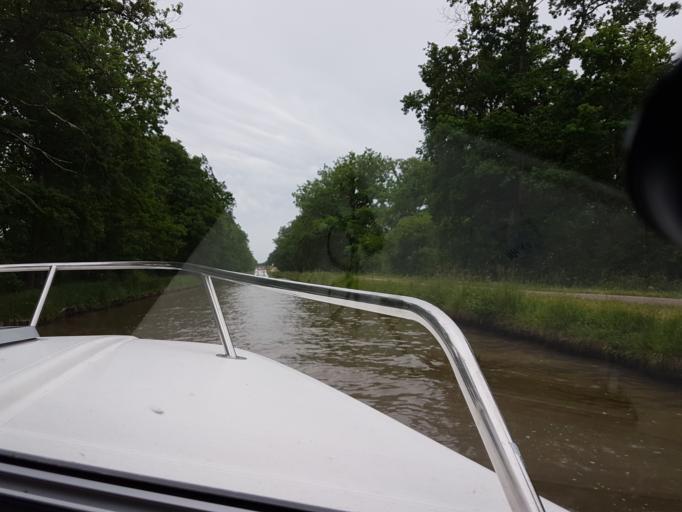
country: FR
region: Bourgogne
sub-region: Departement de la Nievre
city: Clamecy
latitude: 47.3831
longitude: 3.6017
